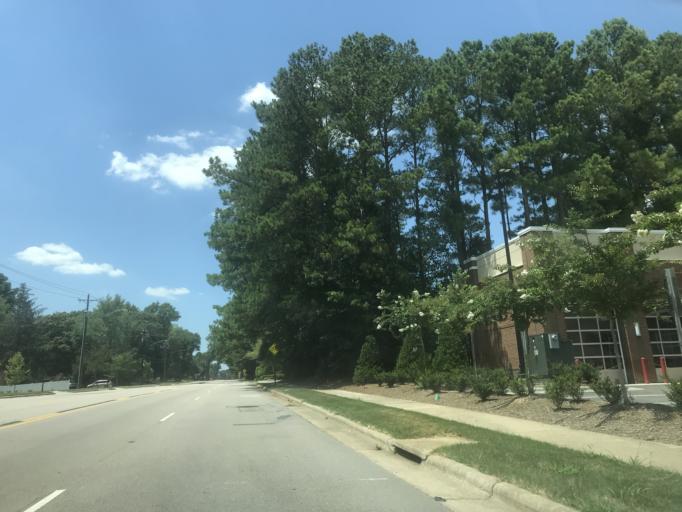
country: US
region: North Carolina
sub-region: Wake County
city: Cary
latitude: 35.7762
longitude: -78.7690
